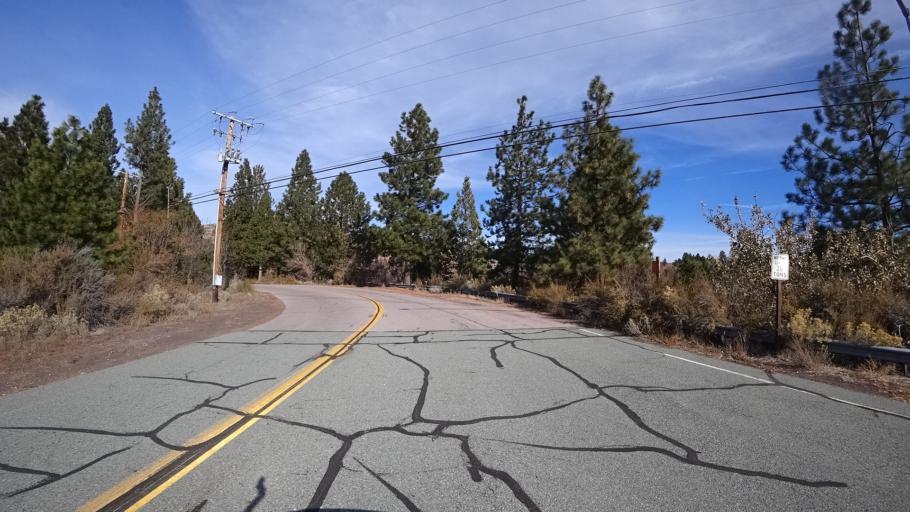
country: US
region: California
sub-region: Siskiyou County
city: Weed
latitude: 41.4246
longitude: -122.3957
